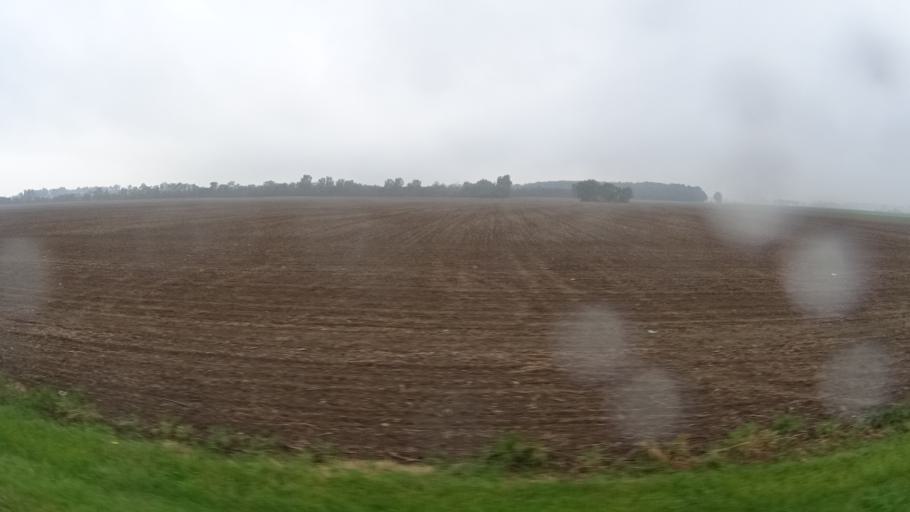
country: US
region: Ohio
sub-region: Huron County
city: Bellevue
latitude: 41.2918
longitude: -82.8416
